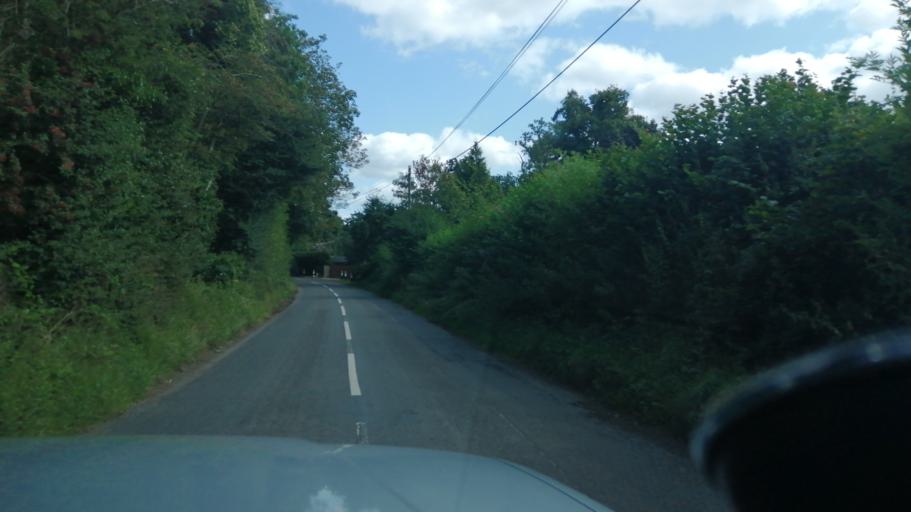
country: GB
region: England
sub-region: Herefordshire
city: Moccas
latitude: 52.0833
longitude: -2.9662
